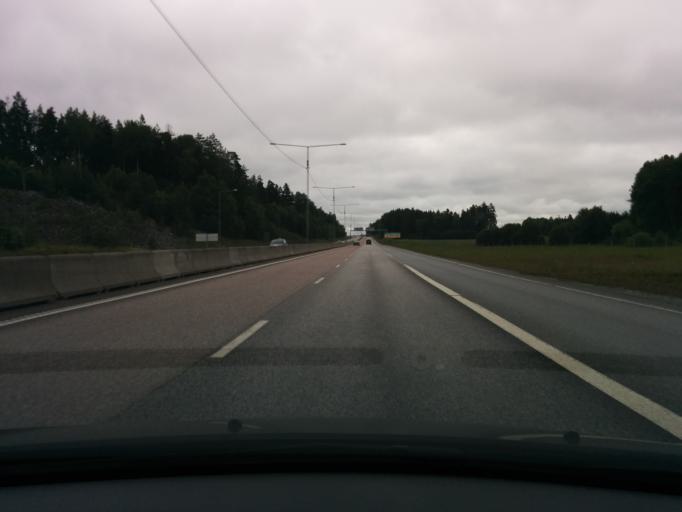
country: SE
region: Stockholm
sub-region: Sigtuna Kommun
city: Rosersberg
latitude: 59.6286
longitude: 17.9218
